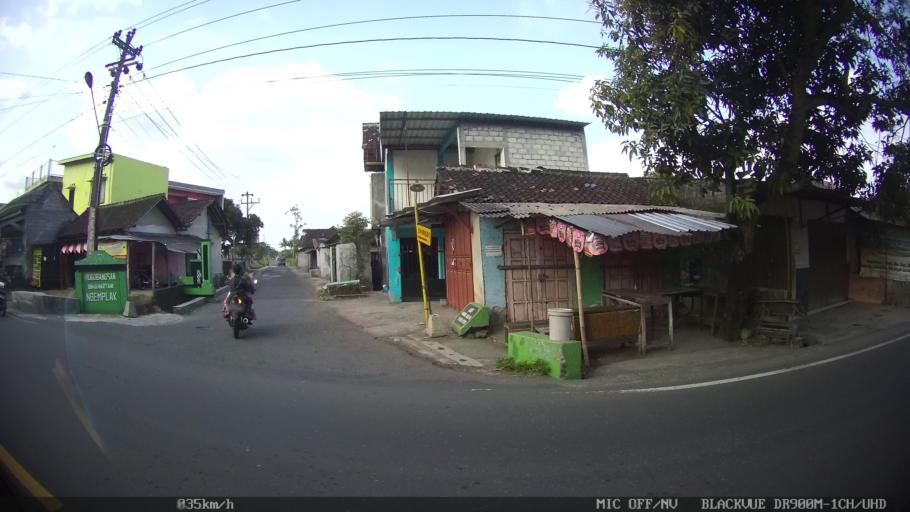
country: ID
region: Central Java
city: Candi Prambanan
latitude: -7.7151
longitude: 110.4721
